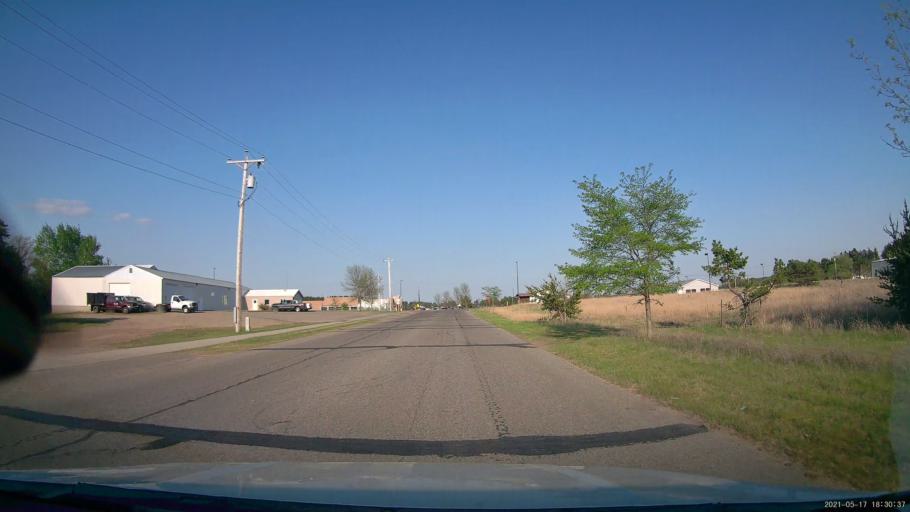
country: US
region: Minnesota
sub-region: Hubbard County
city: Park Rapids
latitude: 46.9247
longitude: -95.0384
